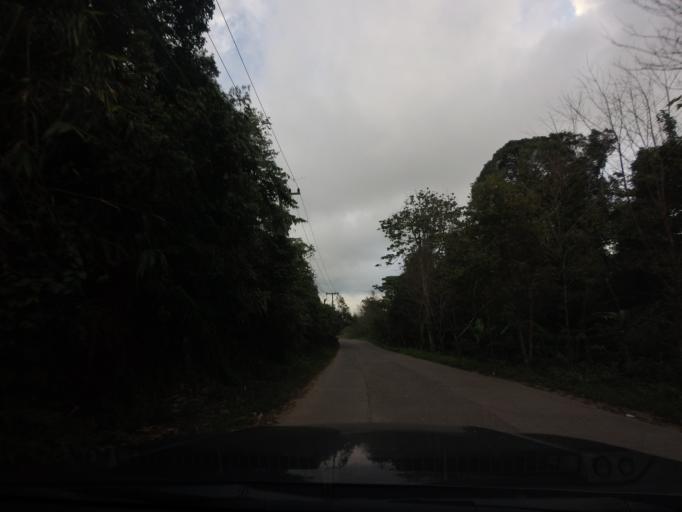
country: TH
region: Phetchabun
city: Lom Kao
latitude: 16.8968
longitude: 101.1043
